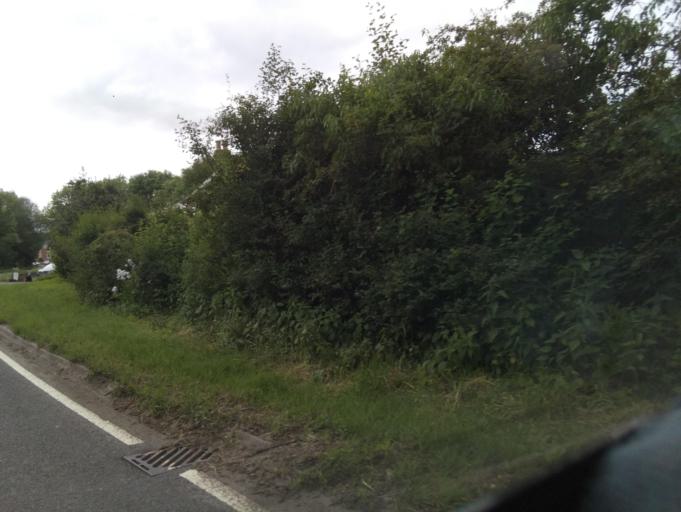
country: GB
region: England
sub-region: Worcestershire
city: Great Malvern
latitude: 52.1298
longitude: -2.3813
